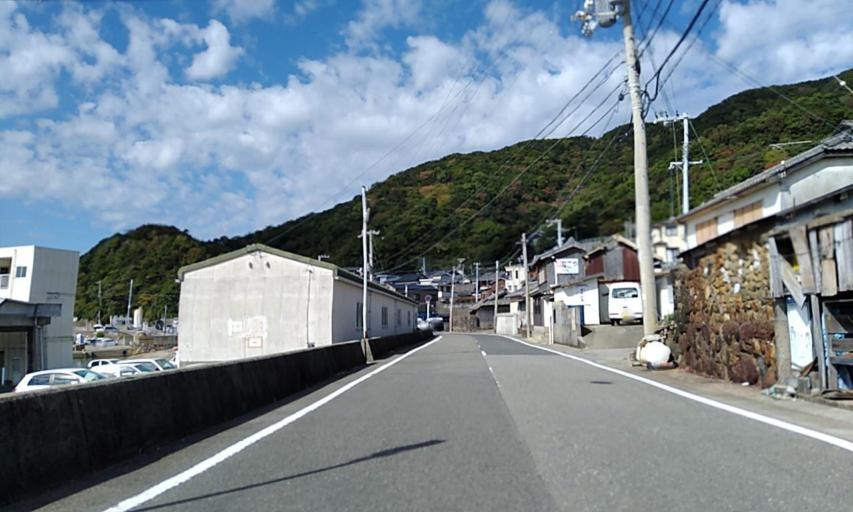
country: JP
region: Wakayama
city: Gobo
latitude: 33.9697
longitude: 135.0854
